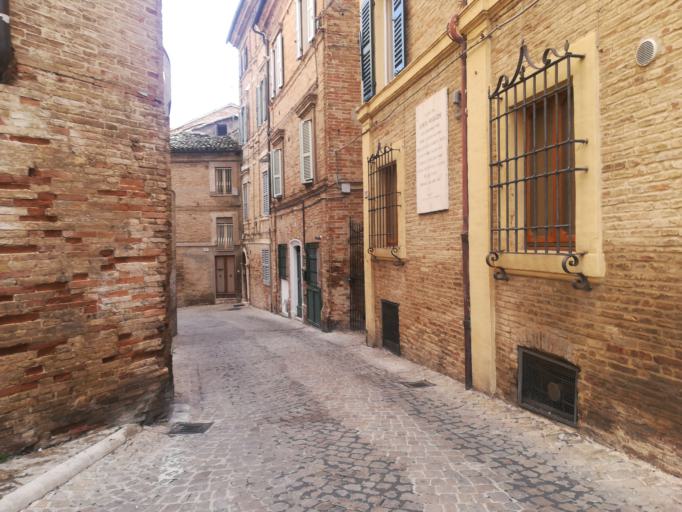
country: IT
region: The Marches
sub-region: Provincia di Macerata
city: Macerata
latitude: 43.3006
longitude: 13.4572
